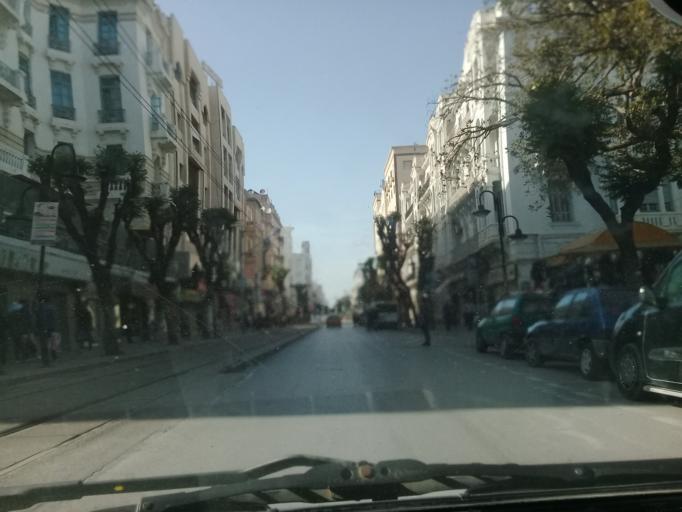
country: TN
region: Tunis
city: Tunis
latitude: 36.8041
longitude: 10.1808
